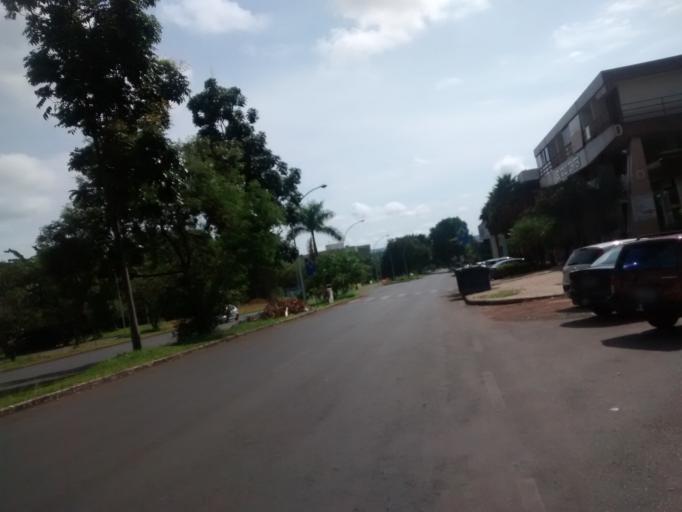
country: BR
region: Federal District
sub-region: Brasilia
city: Brasilia
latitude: -15.7381
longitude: -47.8978
